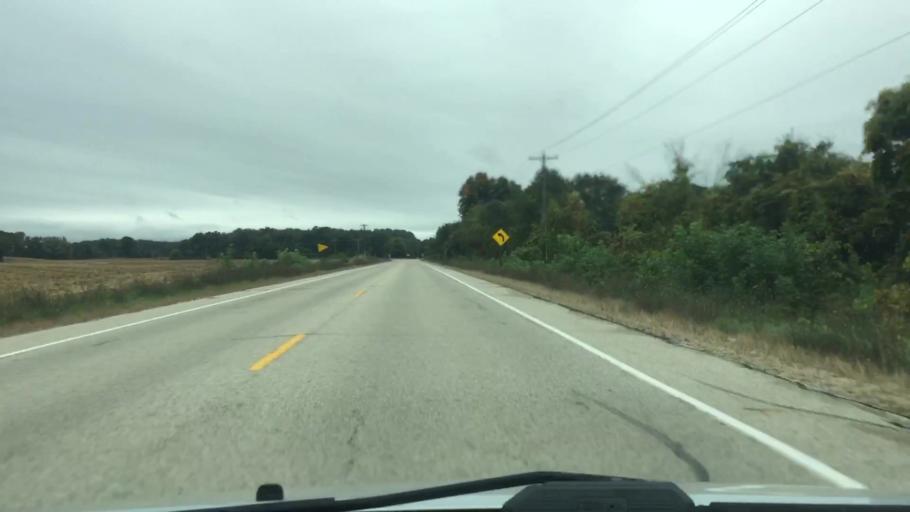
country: US
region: Wisconsin
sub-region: Jefferson County
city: Palmyra
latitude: 42.8208
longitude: -88.5587
